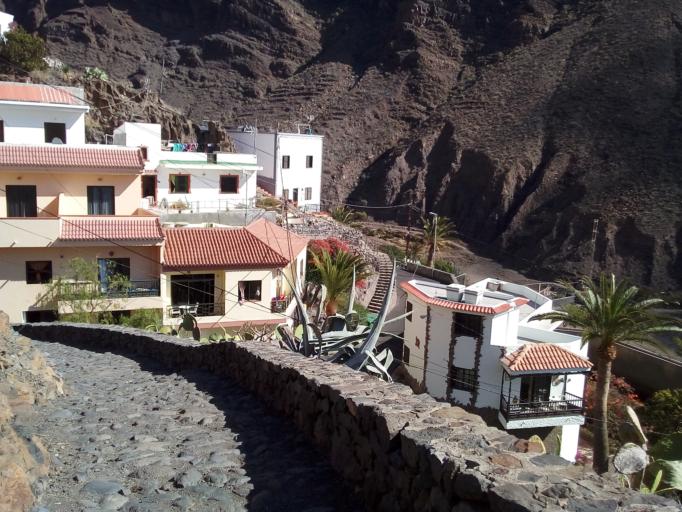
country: ES
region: Canary Islands
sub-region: Provincia de Santa Cruz de Tenerife
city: Alajero
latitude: 28.0980
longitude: -17.3336
